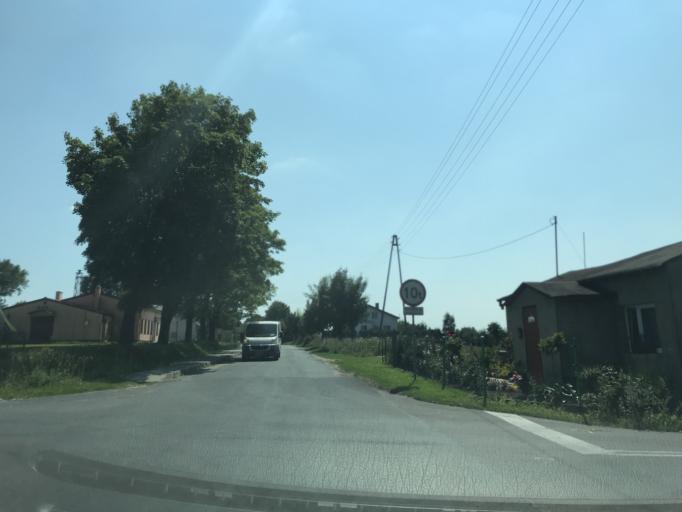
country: PL
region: Kujawsko-Pomorskie
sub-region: Powiat lipnowski
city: Kikol
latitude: 52.9150
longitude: 19.1721
